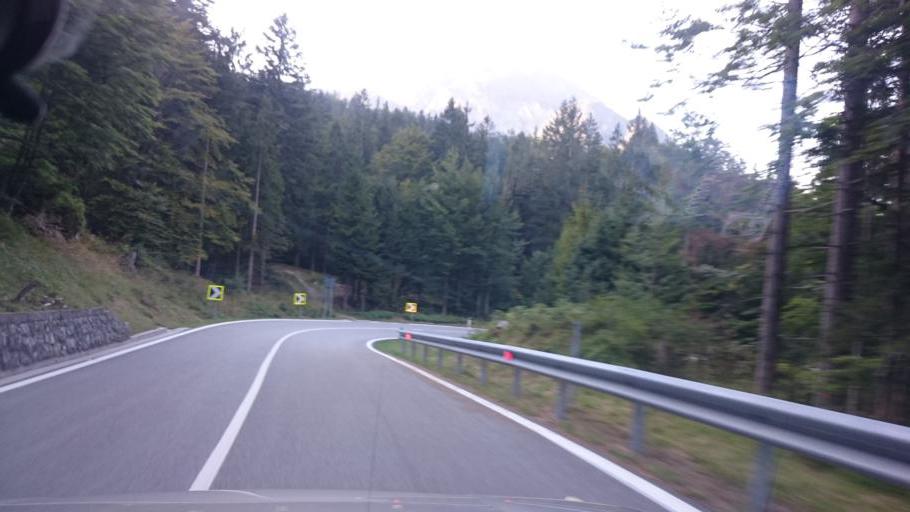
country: IT
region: Friuli Venezia Giulia
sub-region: Provincia di Udine
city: Tarvisio
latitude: 46.4302
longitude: 13.5665
